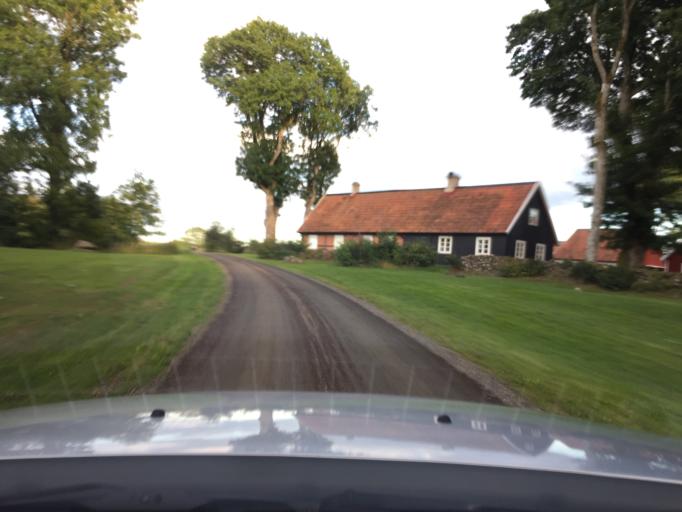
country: SE
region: Skane
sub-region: Hassleholms Kommun
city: Sosdala
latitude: 56.0313
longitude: 13.7164
